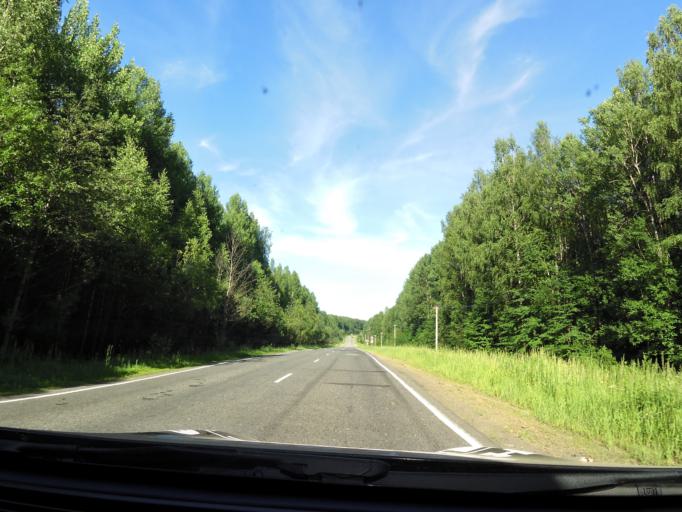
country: RU
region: Kirov
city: Belaya Kholunitsa
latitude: 58.9185
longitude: 51.1037
